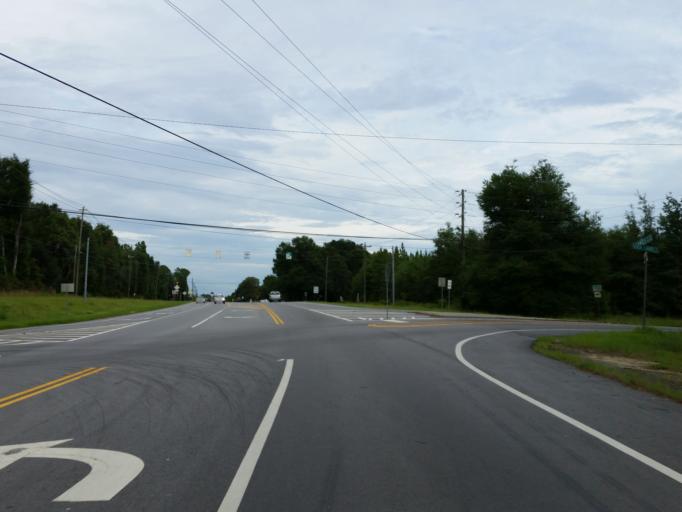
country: US
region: Georgia
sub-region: Lowndes County
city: Valdosta
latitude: 30.6810
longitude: -83.2364
